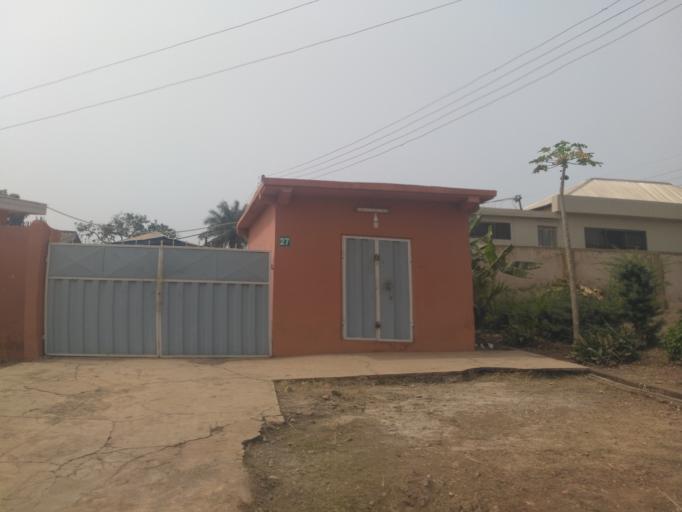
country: GH
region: Ashanti
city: Kumasi
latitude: 6.6970
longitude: -1.6384
